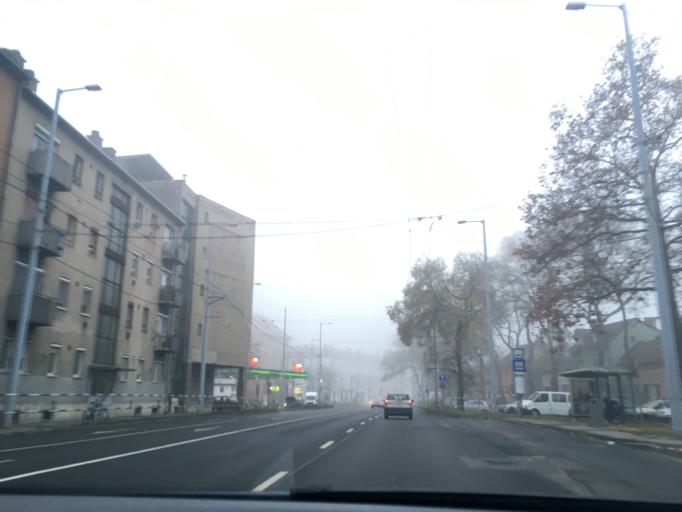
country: HU
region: Hajdu-Bihar
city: Debrecen
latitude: 47.5336
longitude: 21.6394
